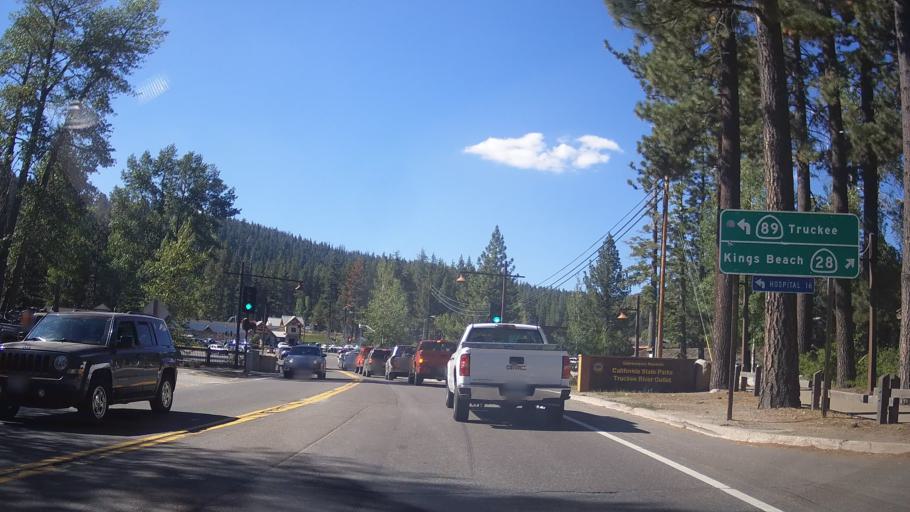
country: US
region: California
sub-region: Placer County
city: Sunnyside-Tahoe City
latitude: 39.1663
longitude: -120.1440
